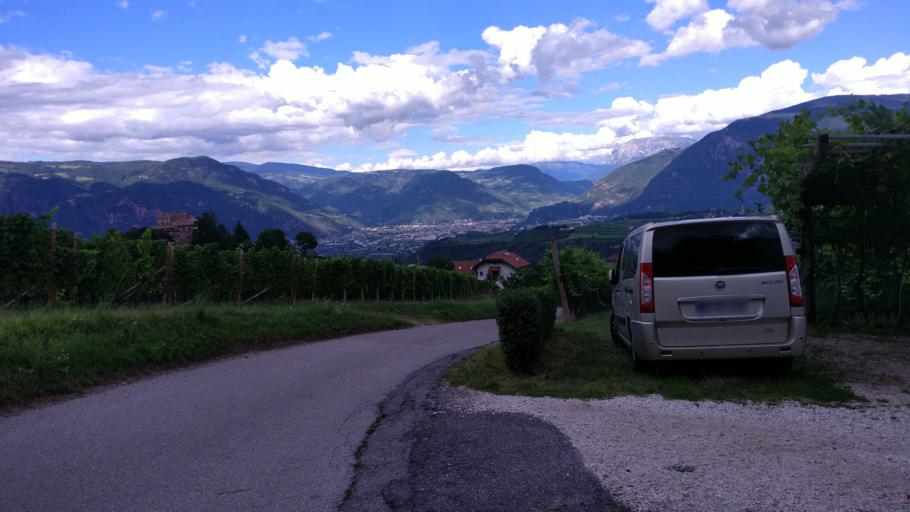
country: IT
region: Trentino-Alto Adige
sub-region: Bolzano
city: San Michele
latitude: 46.4595
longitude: 11.2430
